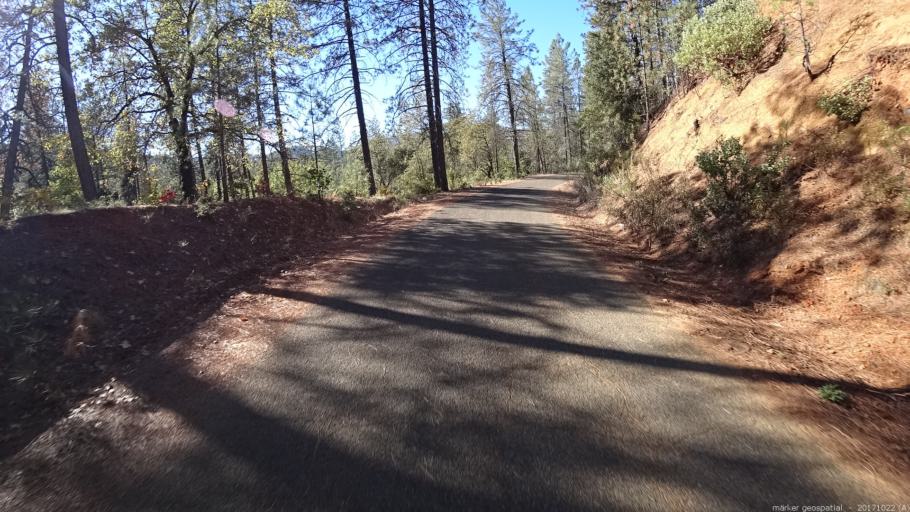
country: US
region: California
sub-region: Shasta County
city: Shasta Lake
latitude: 40.8819
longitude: -122.3679
